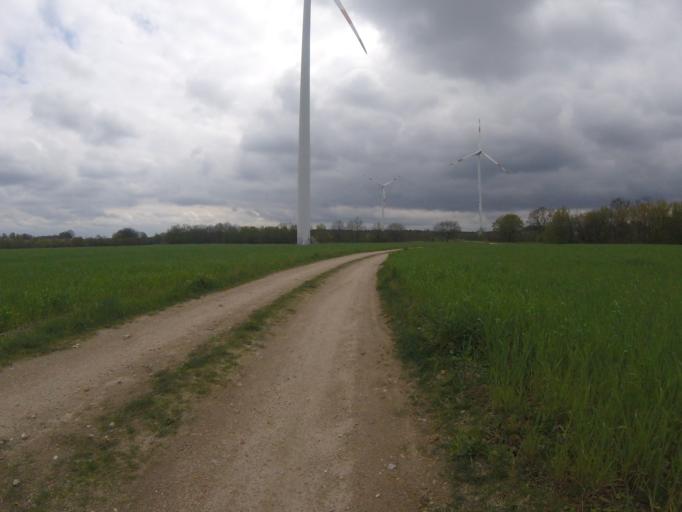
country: DE
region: Brandenburg
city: Mittenwalde
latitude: 52.2491
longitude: 13.5841
